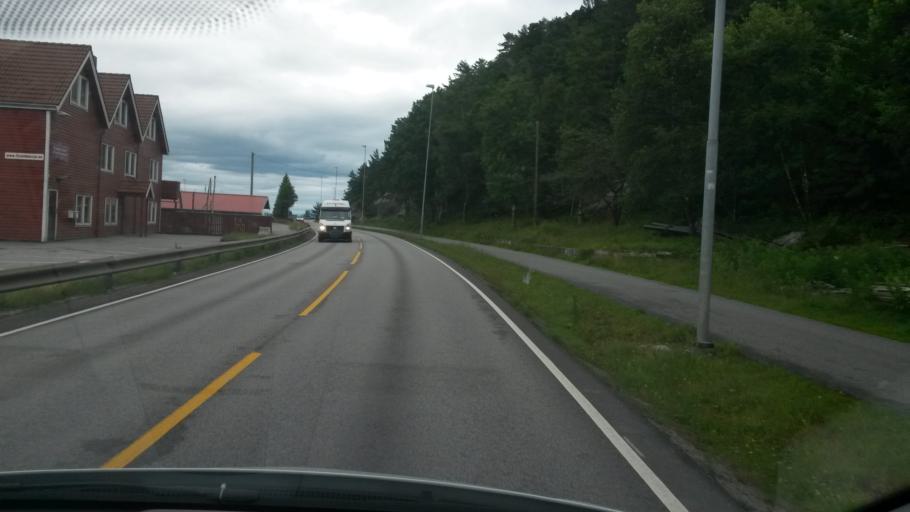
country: NO
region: Rogaland
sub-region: Sandnes
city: Sandnes
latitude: 58.8641
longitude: 5.7559
